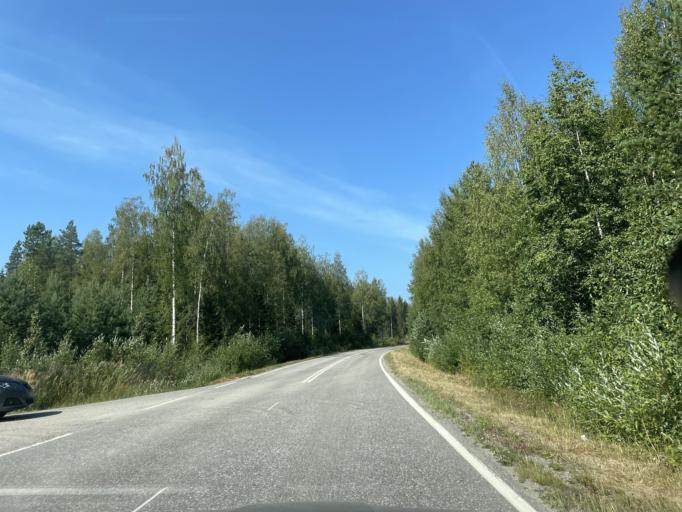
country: FI
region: Central Finland
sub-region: Saarijaervi-Viitasaari
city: Pihtipudas
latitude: 63.3670
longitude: 25.6302
